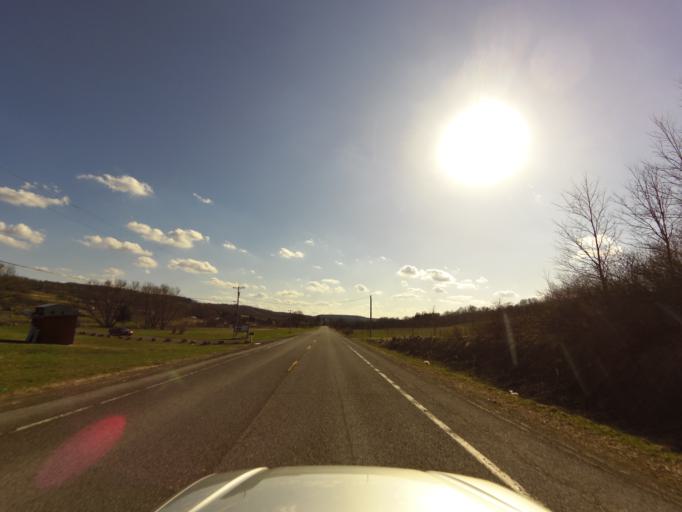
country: US
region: New York
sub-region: Cattaraugus County
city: Franklinville
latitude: 42.3781
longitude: -78.3925
